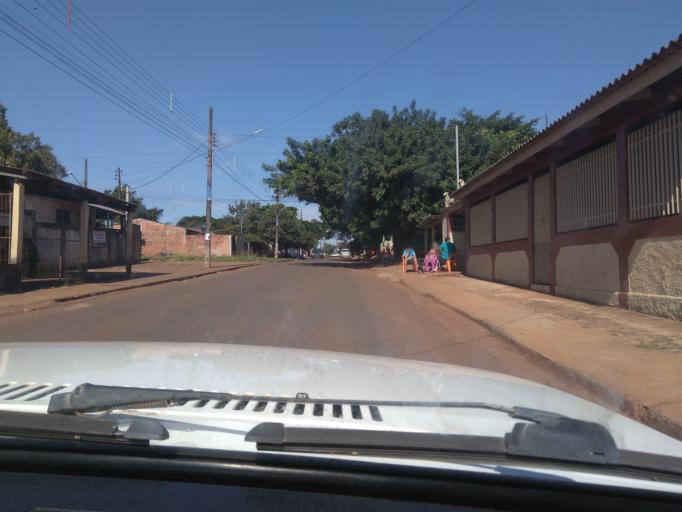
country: BR
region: Mato Grosso do Sul
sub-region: Ponta Pora
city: Ponta Pora
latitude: -22.5169
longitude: -55.7308
